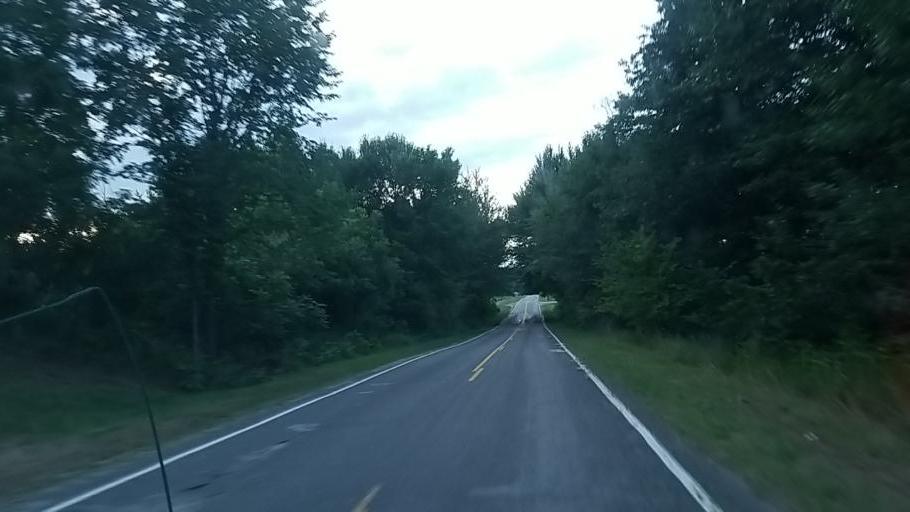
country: US
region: Michigan
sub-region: Newaygo County
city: Fremont
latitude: 43.4804
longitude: -86.0794
